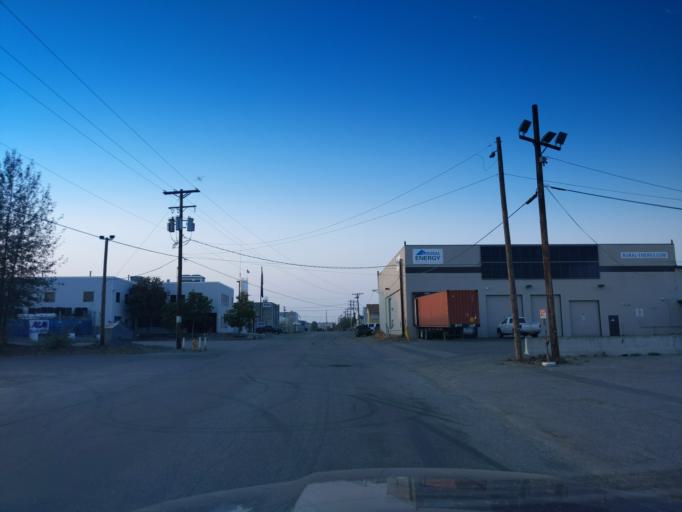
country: US
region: Alaska
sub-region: Anchorage Municipality
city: Anchorage
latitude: 61.1597
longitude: -149.8958
